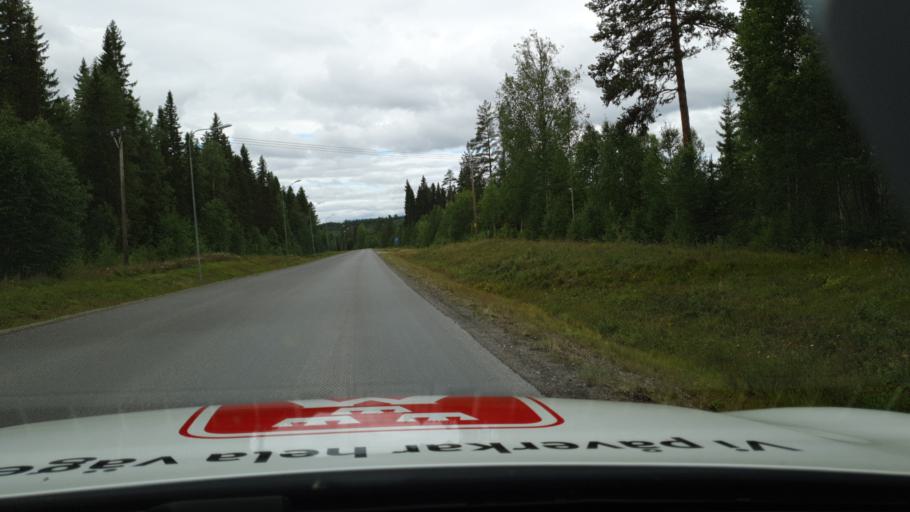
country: SE
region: Vaesterbotten
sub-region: Dorotea Kommun
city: Dorotea
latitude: 64.1259
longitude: 16.2200
